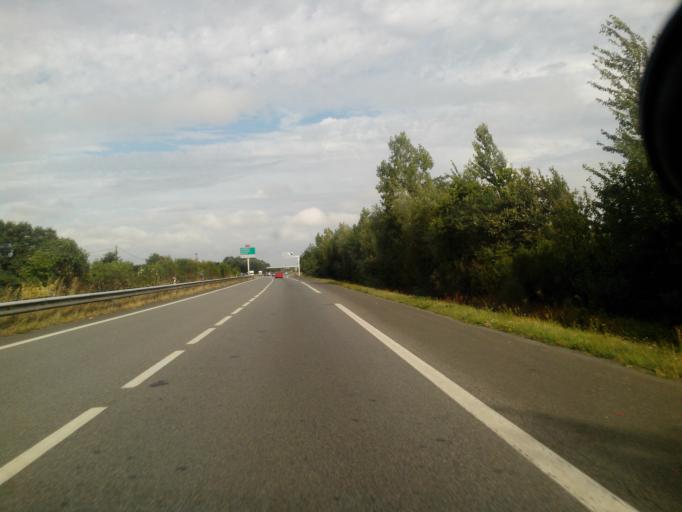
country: FR
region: Pays de la Loire
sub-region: Departement de la Loire-Atlantique
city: La Chapelle-Launay
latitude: 47.3901
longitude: -1.9881
